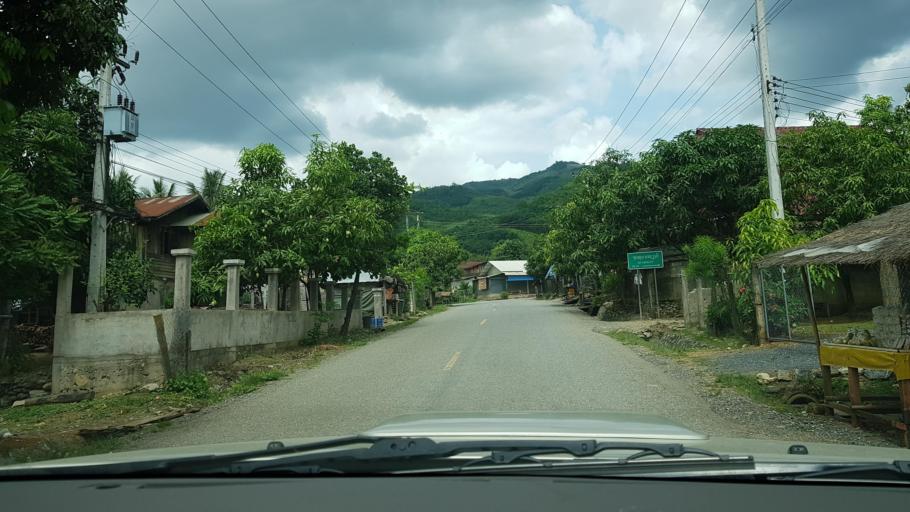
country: LA
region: Loungnamtha
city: Muang Nale
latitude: 20.1554
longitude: 101.5019
